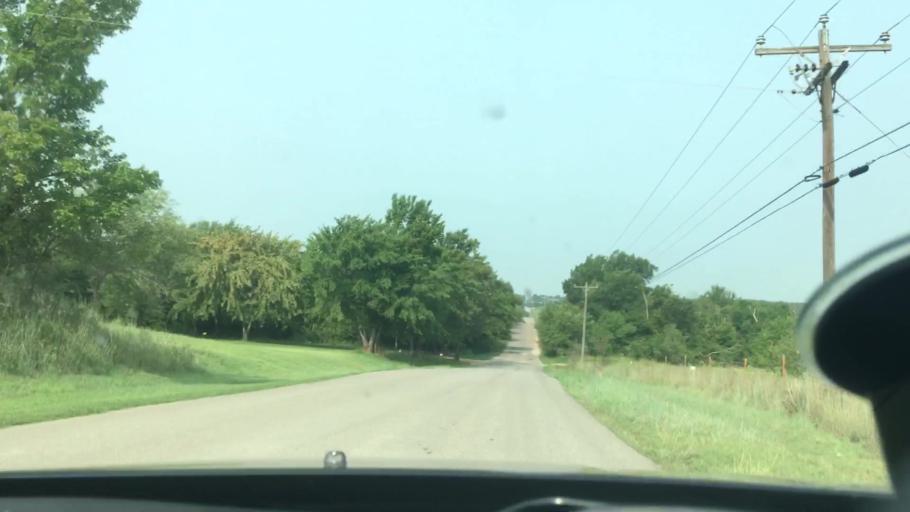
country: US
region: Oklahoma
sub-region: Garvin County
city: Lindsay
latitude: 34.8121
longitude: -97.6509
